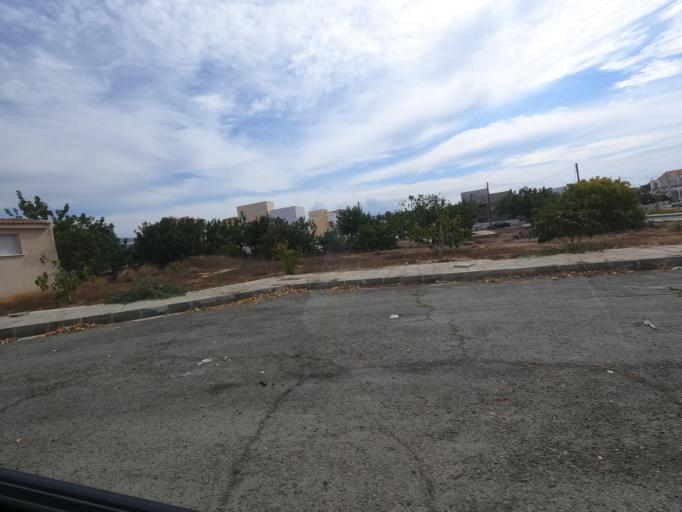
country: CY
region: Pafos
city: Mesogi
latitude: 34.8003
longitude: 32.4446
